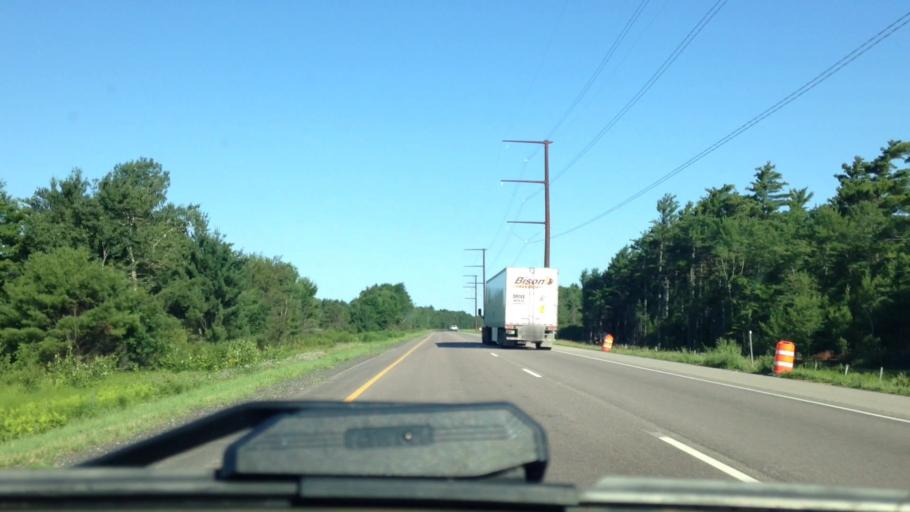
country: US
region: Wisconsin
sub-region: Monroe County
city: Tomah
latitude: 44.1693
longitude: -90.5888
